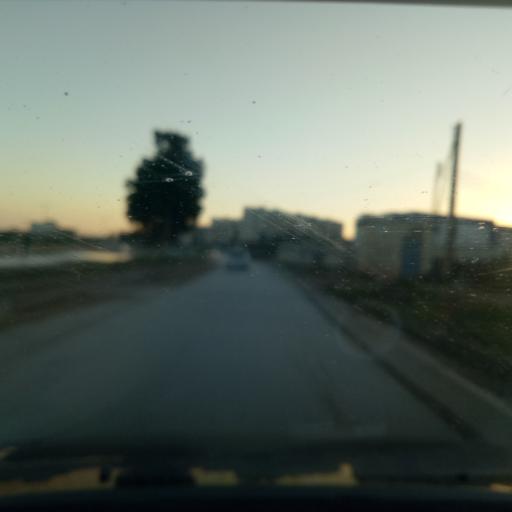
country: DZ
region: Tipaza
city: Bou Ismail
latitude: 36.6411
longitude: 2.7078
